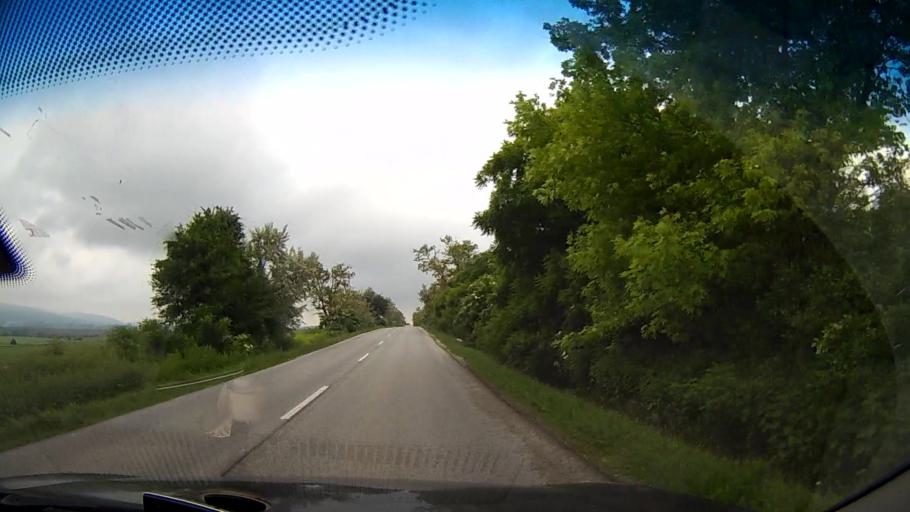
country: HU
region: Pest
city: Perbal
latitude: 47.6017
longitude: 18.7691
